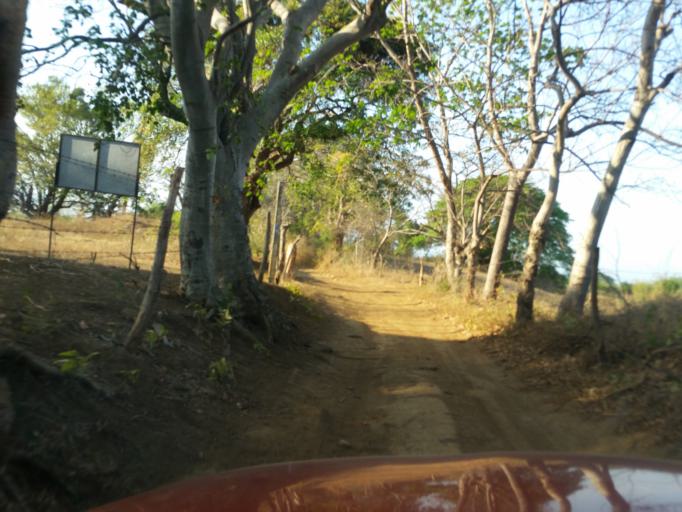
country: NI
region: Managua
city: Managua
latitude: 12.0760
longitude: -86.2582
